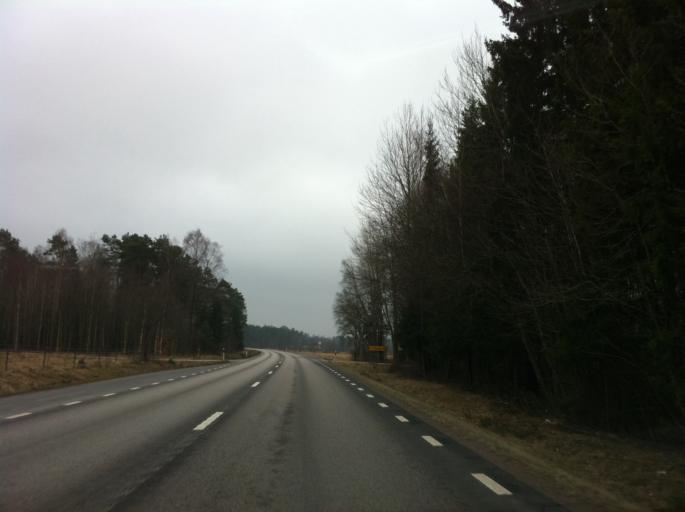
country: SE
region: Vaestra Goetaland
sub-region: Boras Kommun
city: Ganghester
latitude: 57.6698
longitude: 13.0504
